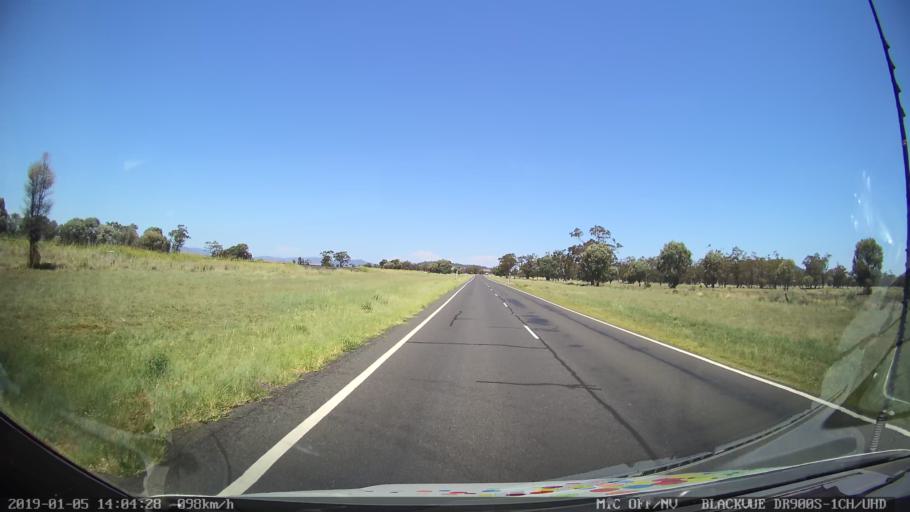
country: AU
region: New South Wales
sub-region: Gunnedah
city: Gunnedah
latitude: -31.2003
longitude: 150.3642
